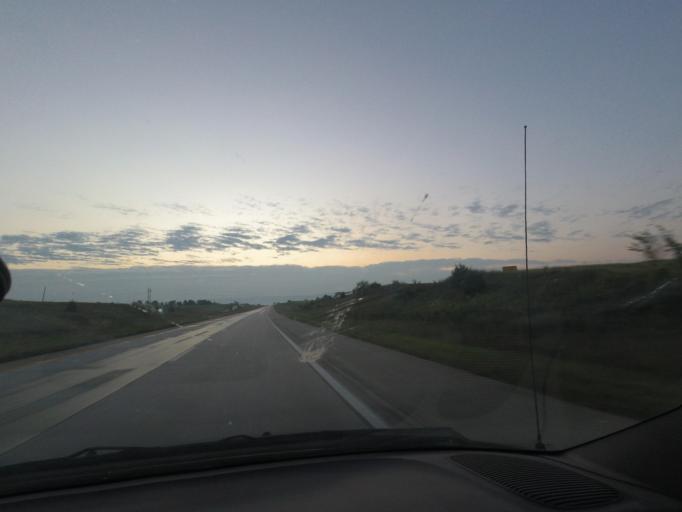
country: US
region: Missouri
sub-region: Linn County
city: Marceline
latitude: 39.7649
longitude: -92.7847
